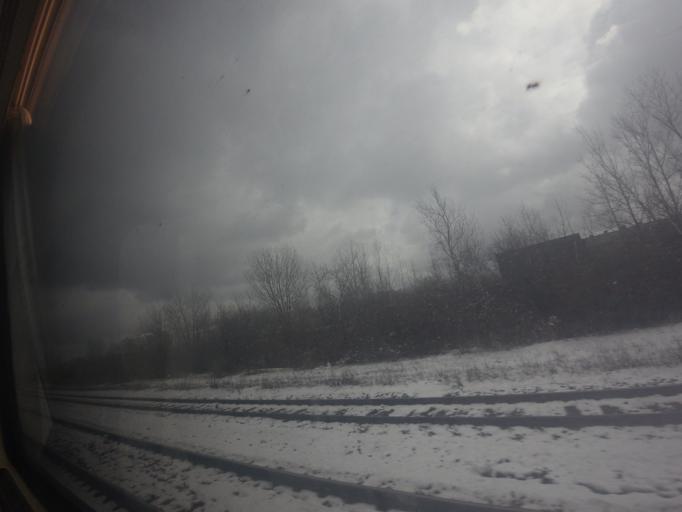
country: CA
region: Ontario
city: Scarborough
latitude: 43.7318
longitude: -79.2441
